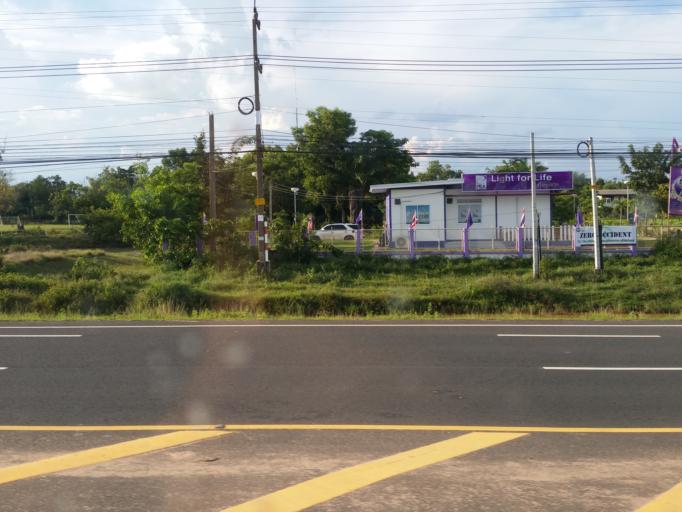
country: TH
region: Changwat Ubon Ratchathani
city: Sirindhorn
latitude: 15.2008
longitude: 105.3872
